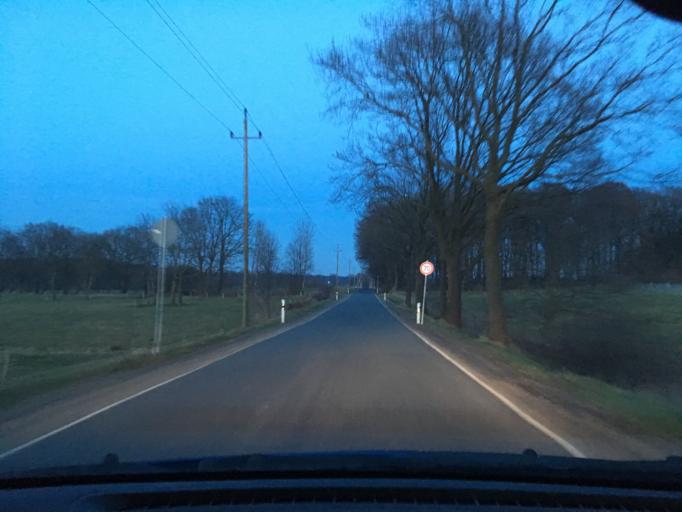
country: DE
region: Lower Saxony
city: Eyendorf
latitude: 53.2010
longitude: 10.1801
